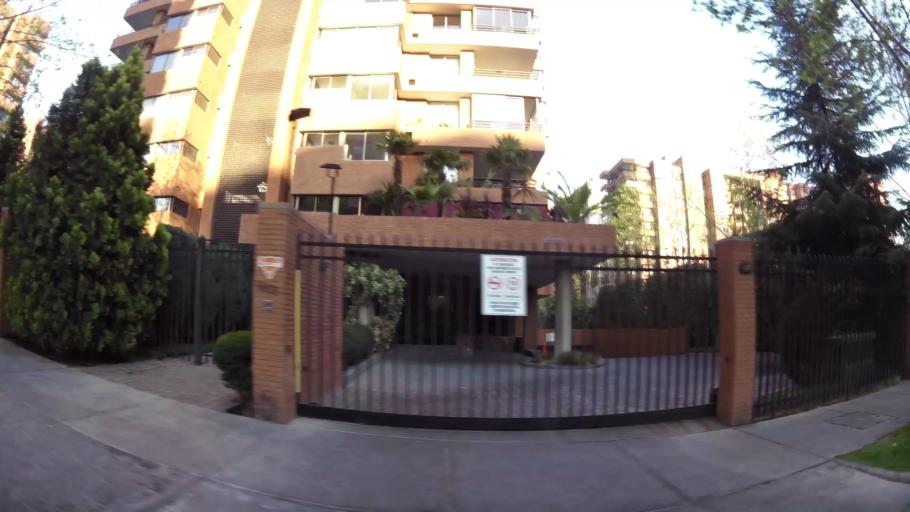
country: CL
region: Santiago Metropolitan
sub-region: Provincia de Santiago
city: Villa Presidente Frei, Nunoa, Santiago, Chile
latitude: -33.4041
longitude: -70.5629
